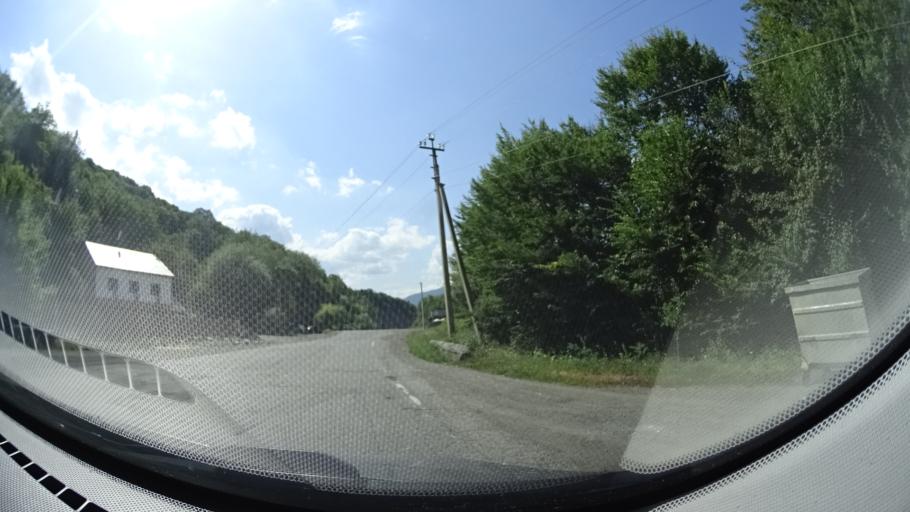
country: GE
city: Zhinvali
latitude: 42.1547
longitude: 44.7238
